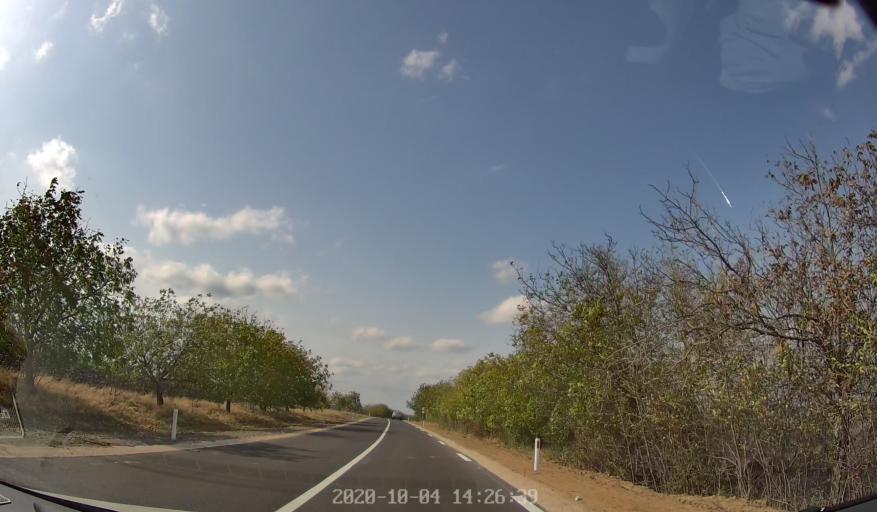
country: MD
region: Rezina
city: Saharna
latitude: 47.6289
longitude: 28.8810
